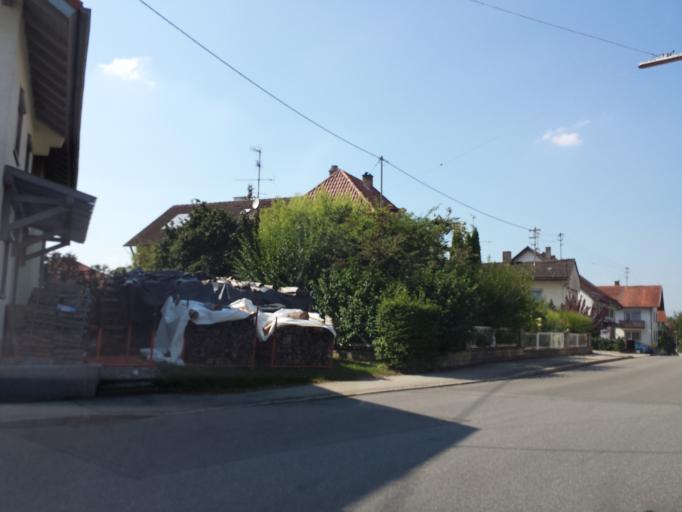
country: DE
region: Bavaria
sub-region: Swabia
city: Tussenhausen
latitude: 48.0853
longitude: 10.5491
